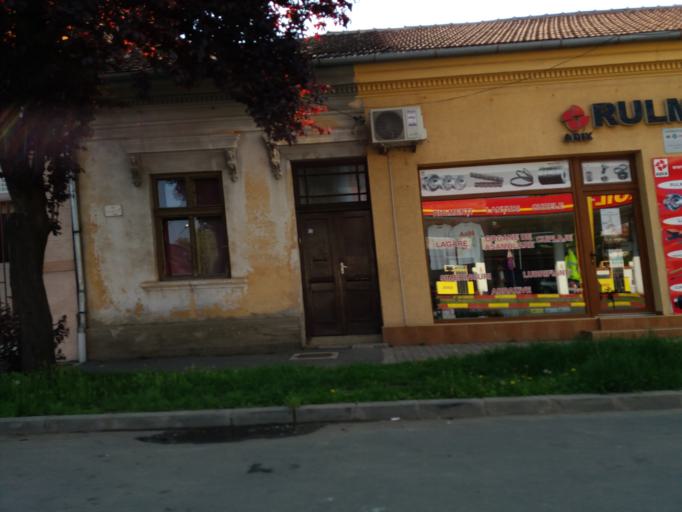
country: RO
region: Arad
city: Arad
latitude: 46.1790
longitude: 21.3083
